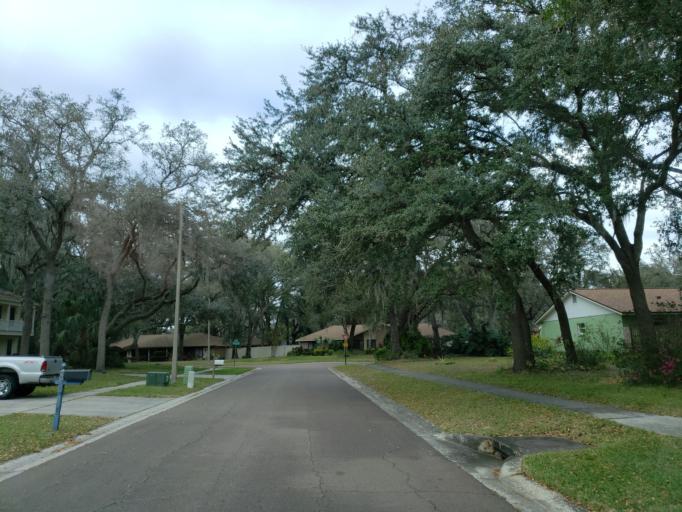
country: US
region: Florida
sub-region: Hillsborough County
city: Bloomingdale
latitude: 27.8826
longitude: -82.2821
